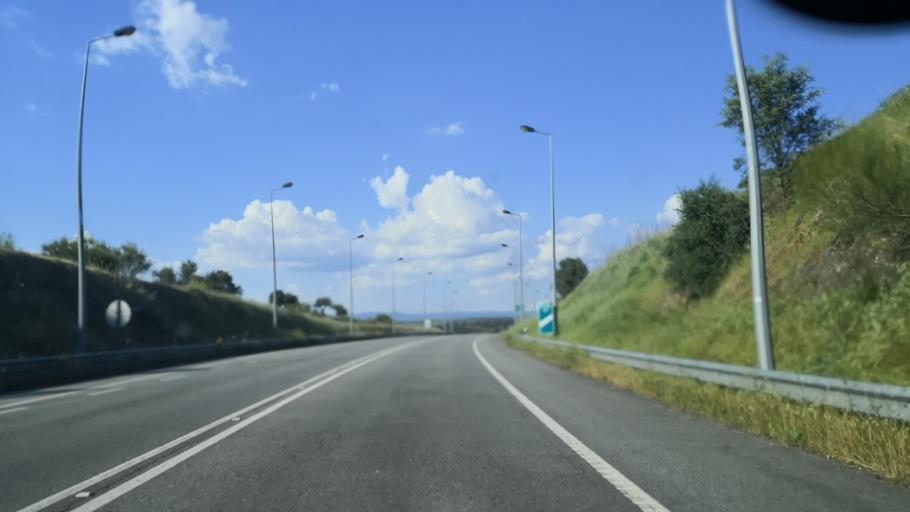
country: PT
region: Portalegre
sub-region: Arronches
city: Arronches
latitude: 39.0518
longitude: -7.4462
